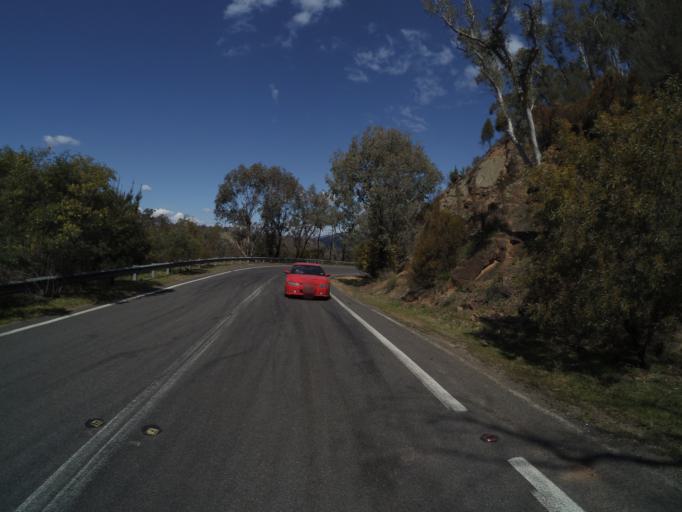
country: AU
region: Australian Capital Territory
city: Macquarie
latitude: -35.3176
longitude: 148.9461
